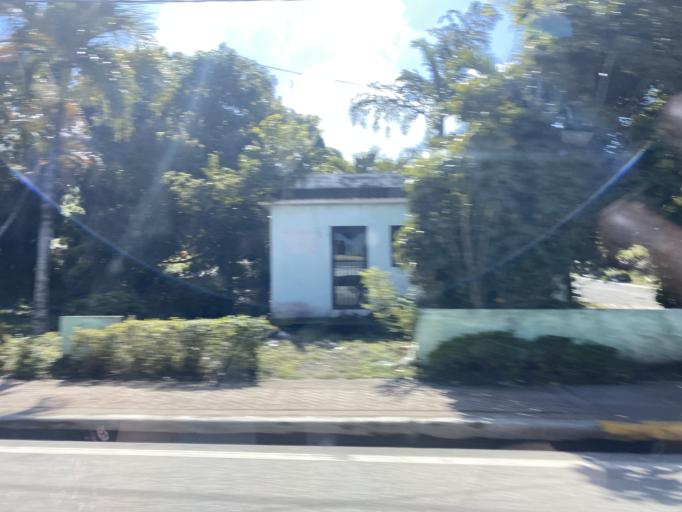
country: DO
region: Puerto Plata
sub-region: Puerto Plata
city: Puerto Plata
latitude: 19.7940
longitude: -70.7126
